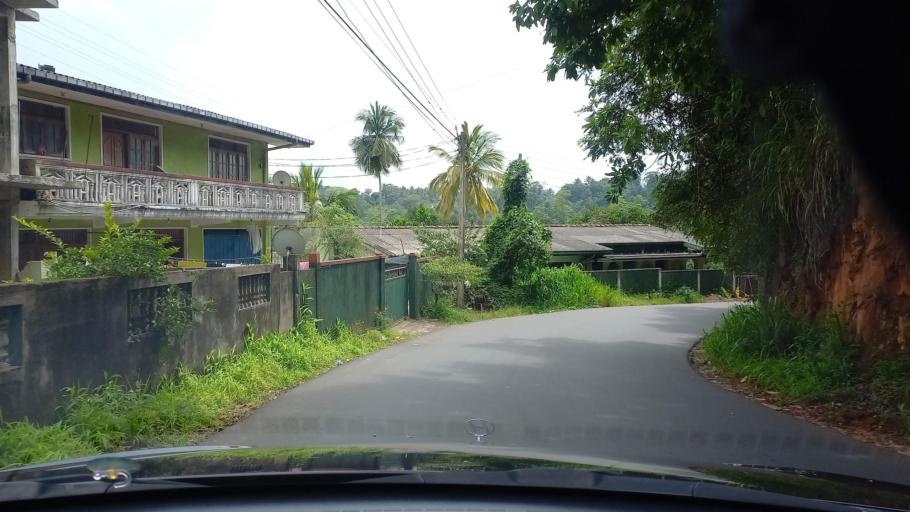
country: LK
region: Central
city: Kandy
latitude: 7.2357
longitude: 80.6032
